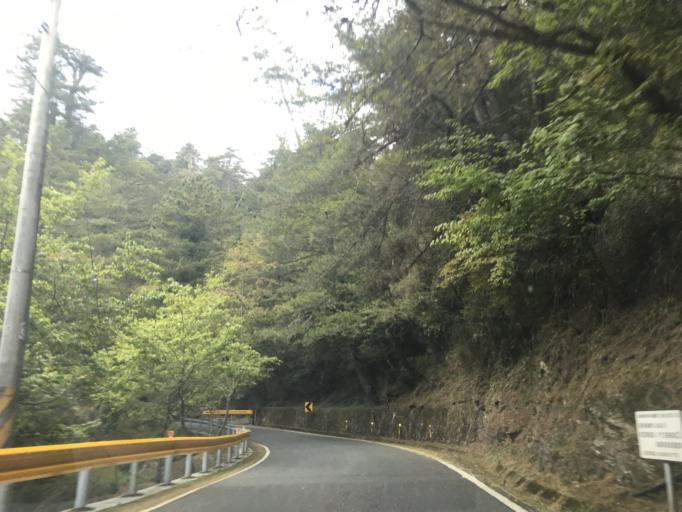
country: TW
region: Taiwan
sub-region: Hualien
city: Hualian
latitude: 24.1822
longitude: 121.3242
